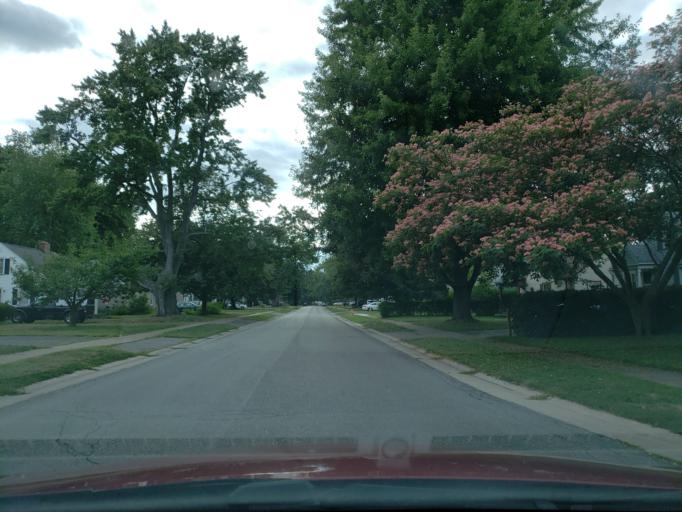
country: US
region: New York
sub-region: Monroe County
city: Greece
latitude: 43.2110
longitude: -77.6478
